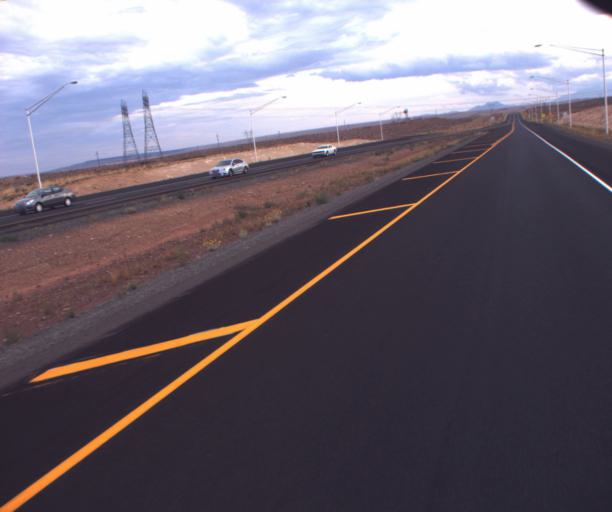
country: US
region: Arizona
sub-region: Coconino County
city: Tuba City
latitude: 35.8376
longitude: -111.4364
